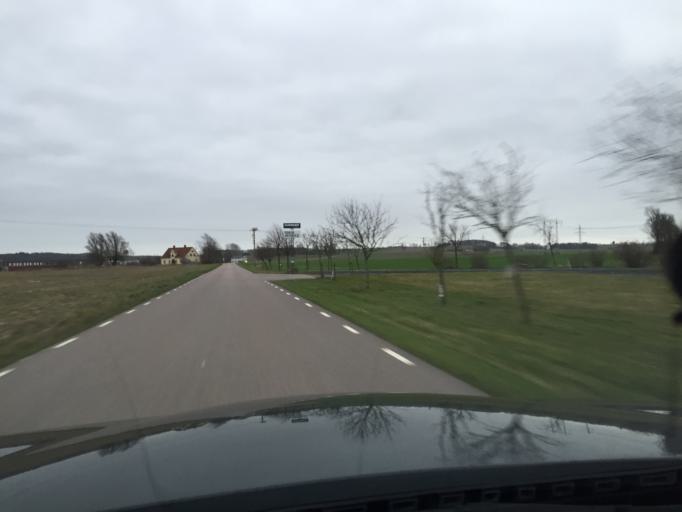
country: SE
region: Skane
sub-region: Malmo
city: Oxie
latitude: 55.5661
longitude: 13.1577
